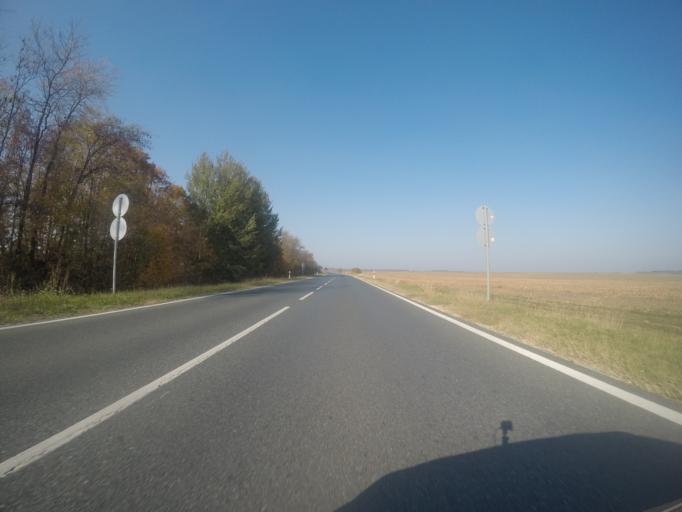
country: HU
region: Tolna
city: Madocsa
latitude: 46.7057
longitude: 18.8884
